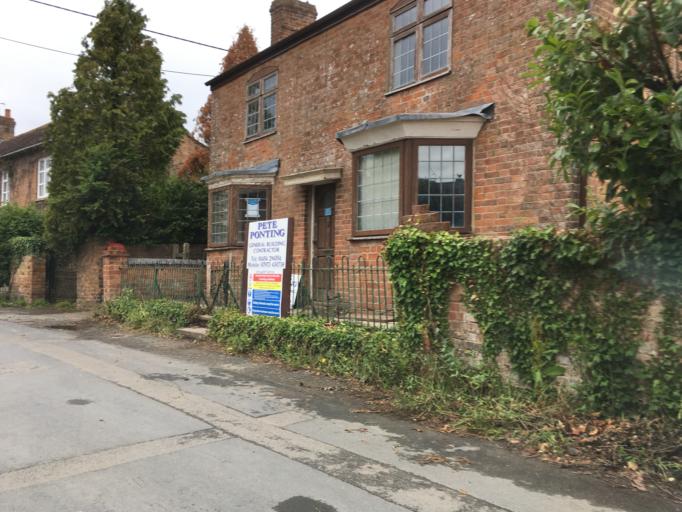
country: GB
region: England
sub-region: Gloucestershire
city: Cinderford
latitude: 51.7963
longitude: -2.4237
